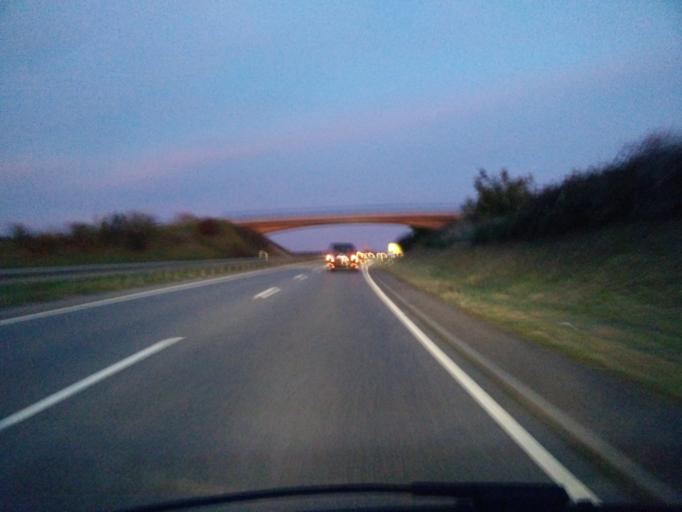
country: DE
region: Baden-Wuerttemberg
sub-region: Regierungsbezirk Stuttgart
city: Rutesheim
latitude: 48.8171
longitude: 8.9420
